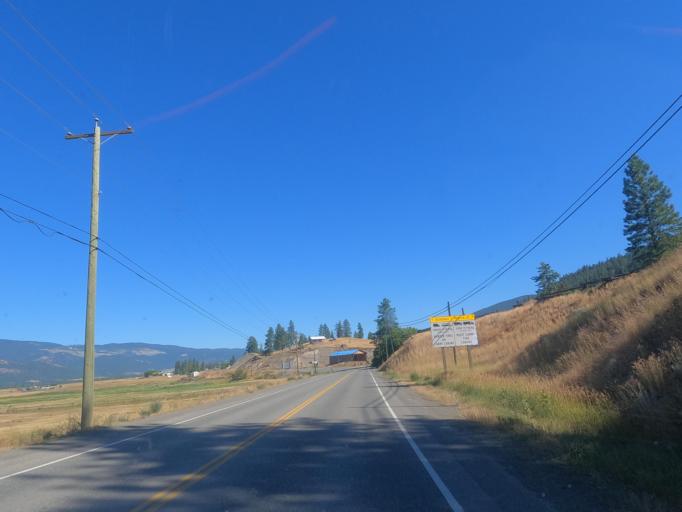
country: CA
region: British Columbia
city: Merritt
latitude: 50.1313
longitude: -120.8337
